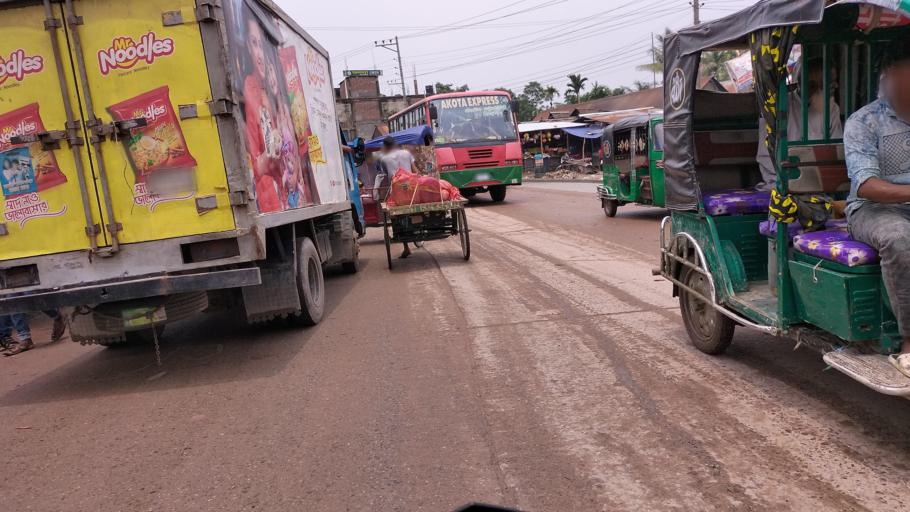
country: BD
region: Dhaka
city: Mymensingh
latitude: 24.7627
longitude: 90.4507
